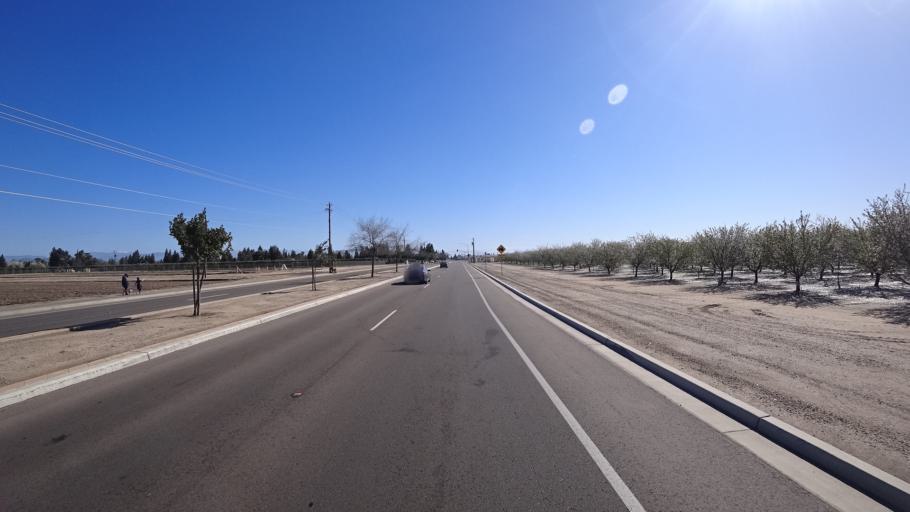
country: US
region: California
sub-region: Fresno County
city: Clovis
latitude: 36.8230
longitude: -119.7337
